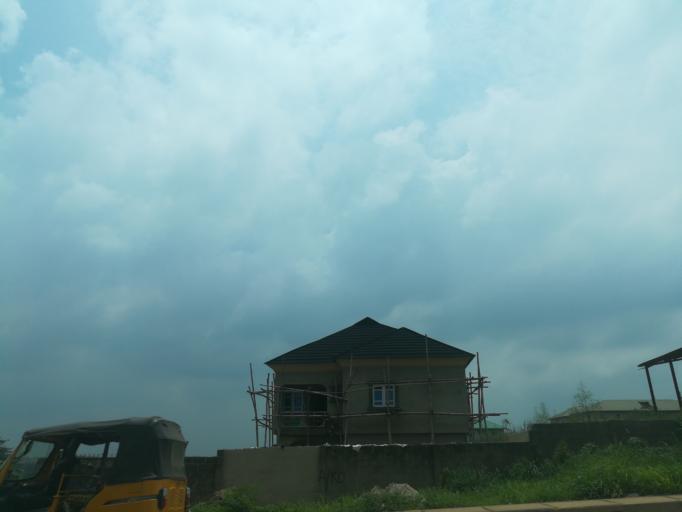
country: NG
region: Lagos
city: Ikorodu
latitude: 6.6294
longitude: 3.5320
